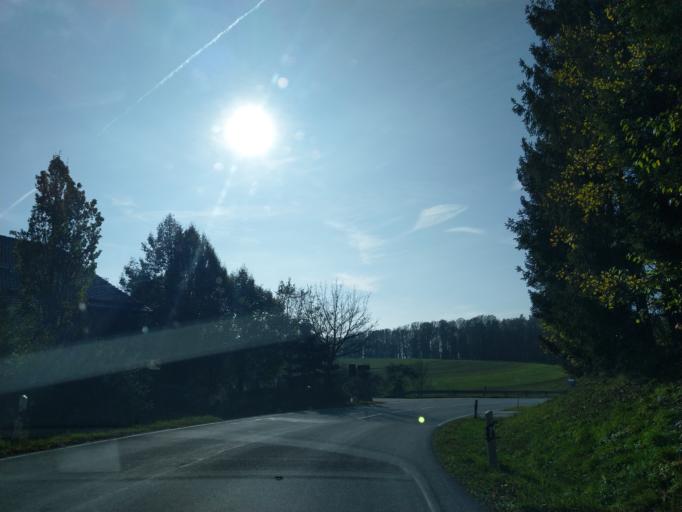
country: DE
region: Bavaria
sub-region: Lower Bavaria
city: Grattersdorf
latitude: 48.8012
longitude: 13.1942
